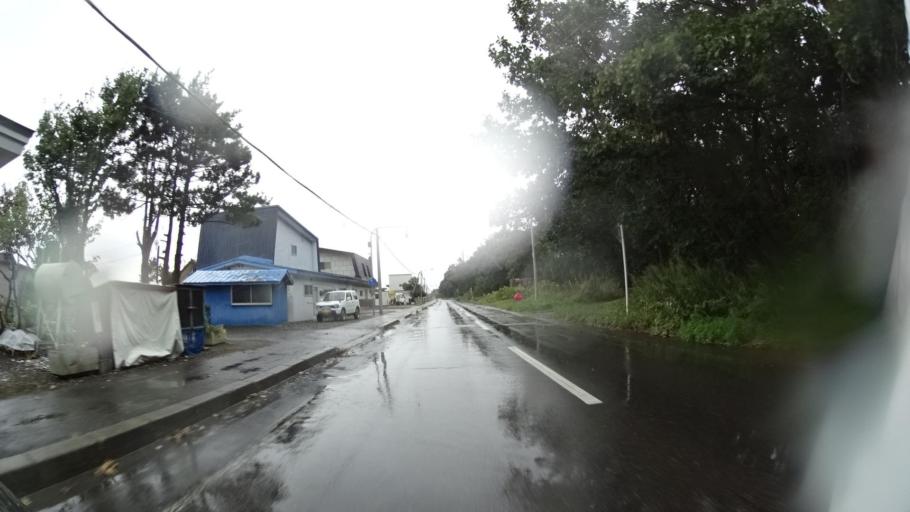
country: JP
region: Hokkaido
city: Mombetsu
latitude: 44.3296
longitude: 143.4941
